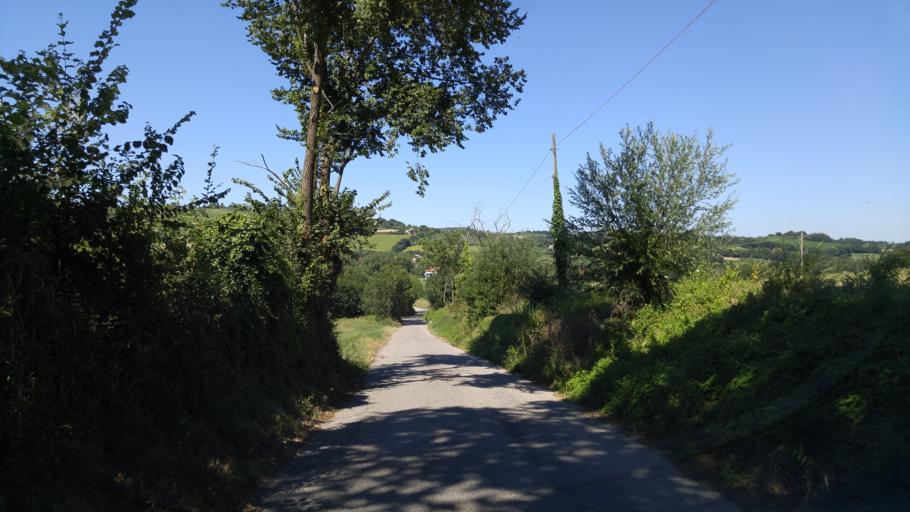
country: IT
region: The Marches
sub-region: Provincia di Pesaro e Urbino
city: Mombaroccio
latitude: 43.8352
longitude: 12.8883
